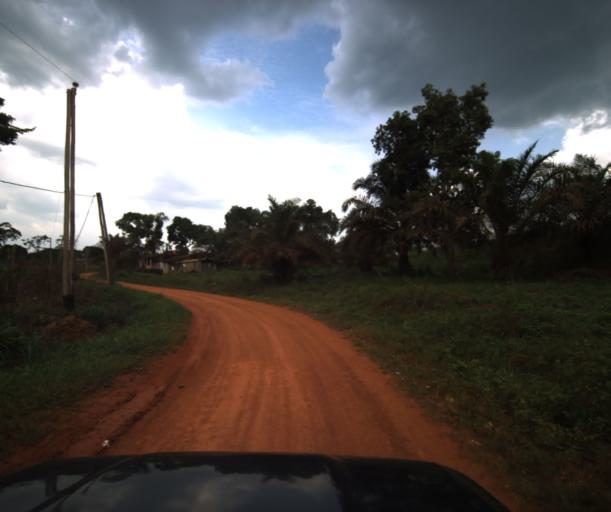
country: CM
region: Centre
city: Akono
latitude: 3.5973
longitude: 11.1777
